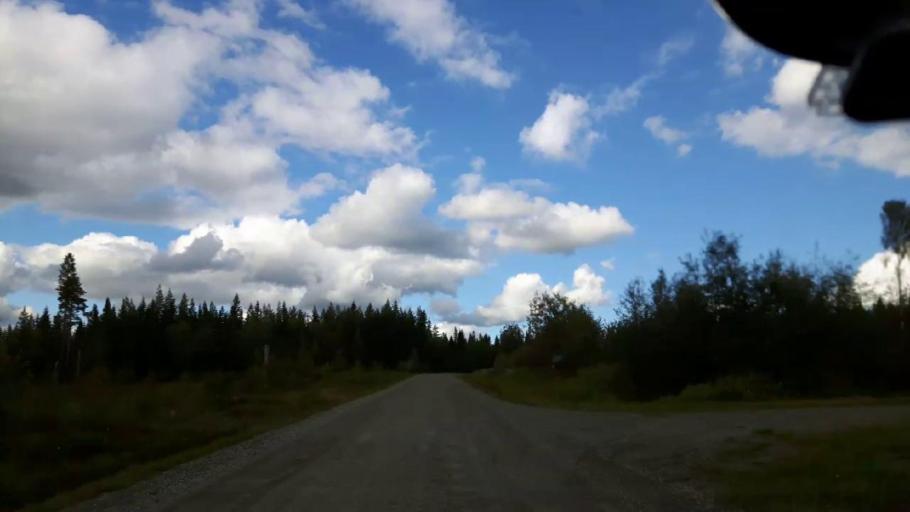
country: SE
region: Jaemtland
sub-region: Stroemsunds Kommun
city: Stroemsund
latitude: 63.4033
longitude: 15.7702
